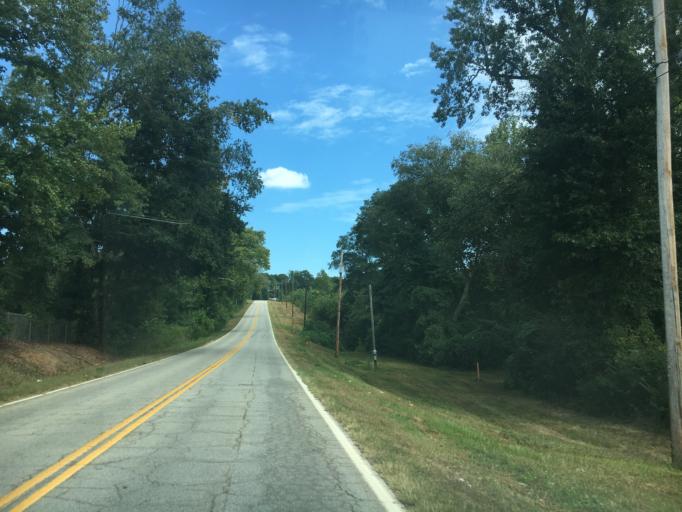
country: US
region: South Carolina
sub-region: Laurens County
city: Watts Mills
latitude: 34.5035
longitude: -81.9885
